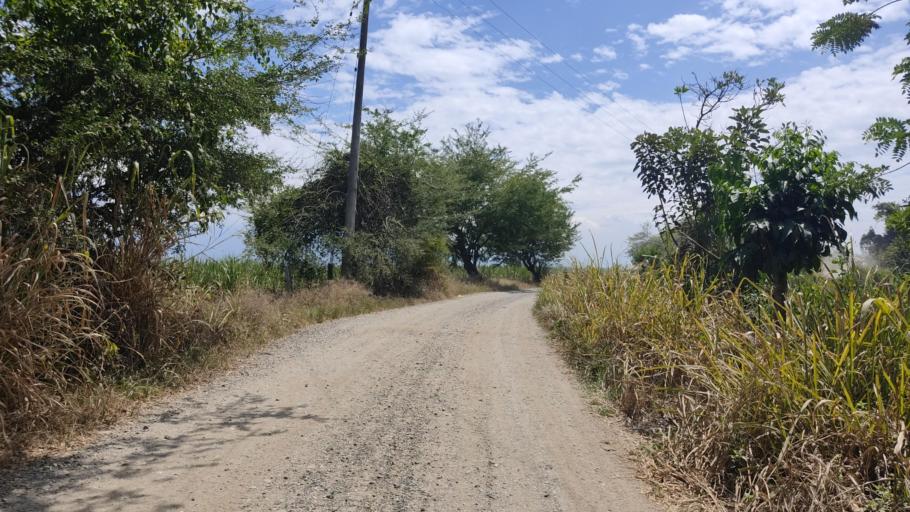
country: CO
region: Valle del Cauca
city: Jamundi
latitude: 3.1569
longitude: -76.5125
